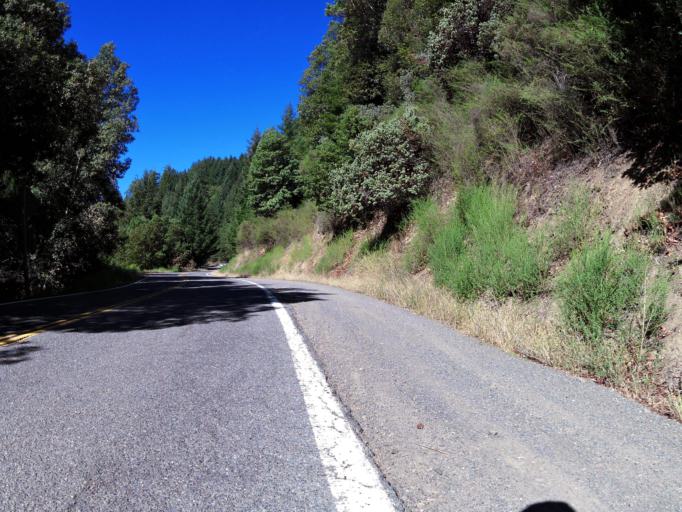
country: US
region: California
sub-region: Humboldt County
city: Redway
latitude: 39.8491
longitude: -123.7355
